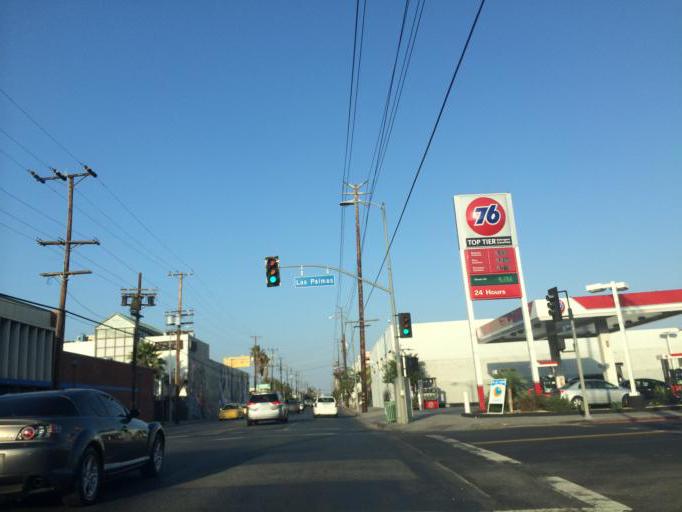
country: US
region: California
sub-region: Los Angeles County
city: Hollywood
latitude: 34.0906
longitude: -118.3364
